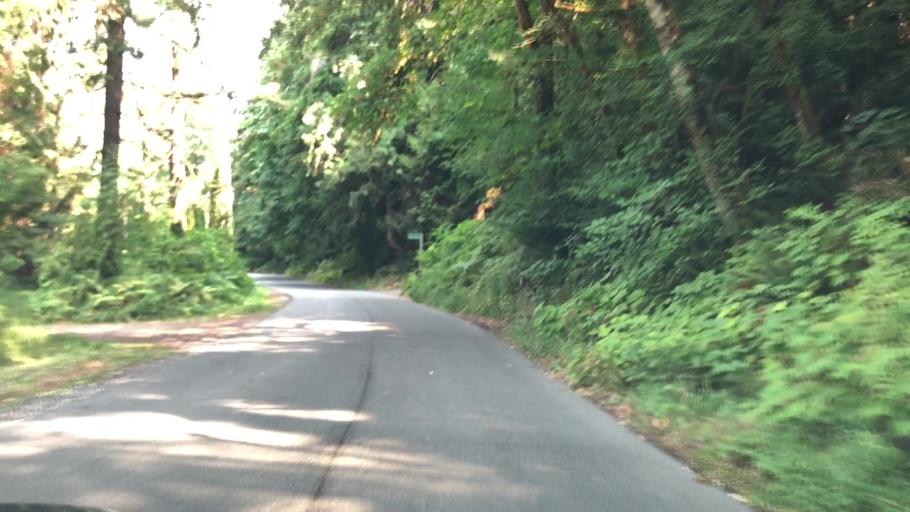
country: US
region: Washington
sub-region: King County
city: Cottage Lake
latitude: 47.7506
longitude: -122.0787
